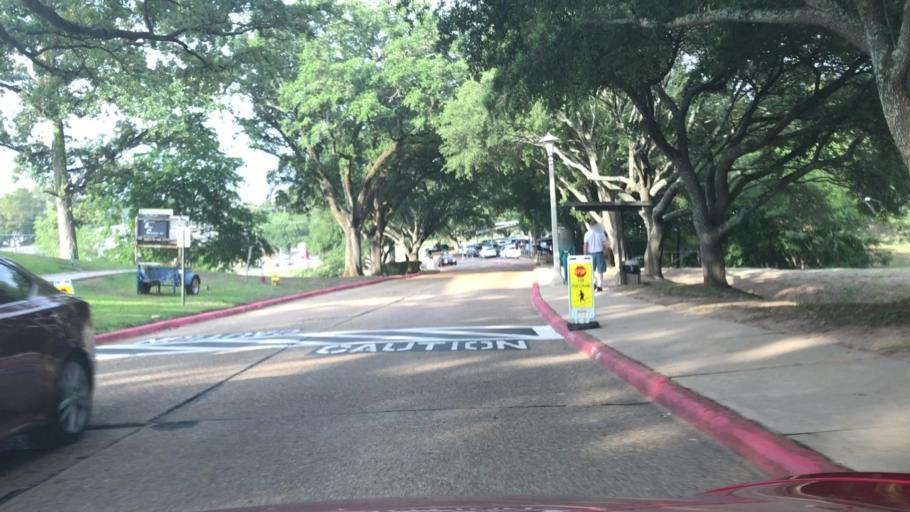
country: US
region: Louisiana
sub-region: Bossier Parish
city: Bossier City
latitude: 32.5015
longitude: -93.7213
